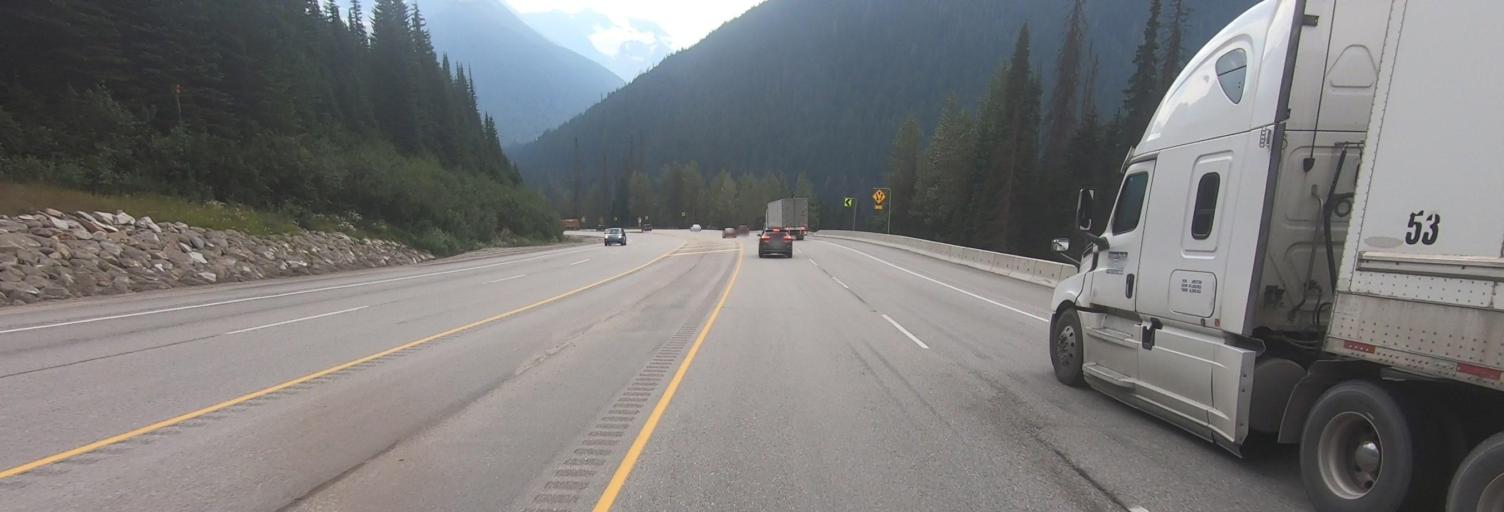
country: CA
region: British Columbia
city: Golden
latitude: 51.2749
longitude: -117.5088
